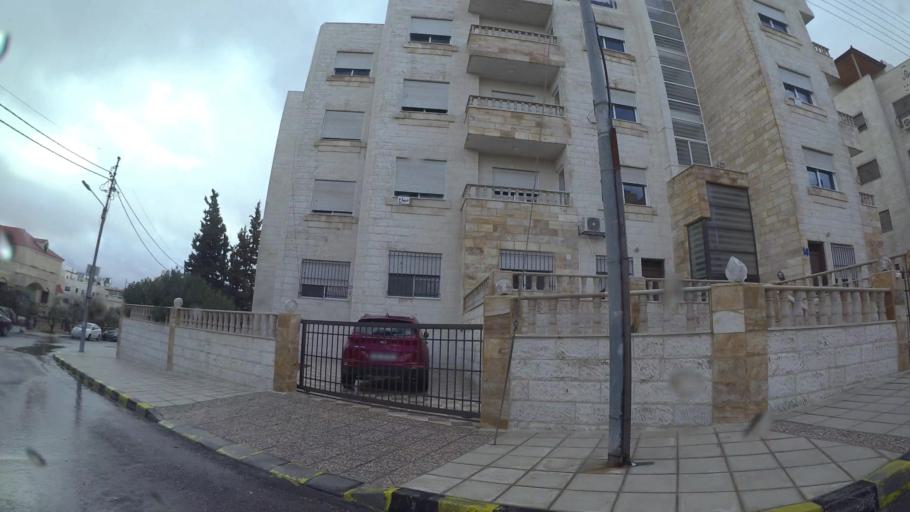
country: JO
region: Amman
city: Al Jubayhah
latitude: 32.0320
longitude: 35.8692
